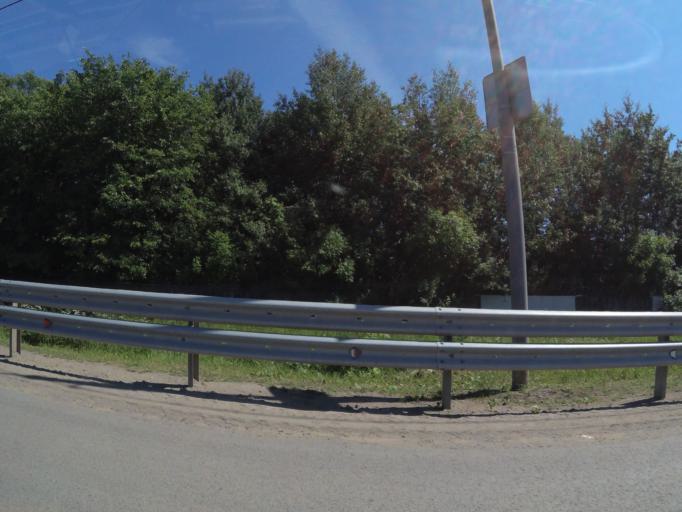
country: RU
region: Moskovskaya
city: Novopodrezkovo
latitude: 55.9756
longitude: 37.3835
